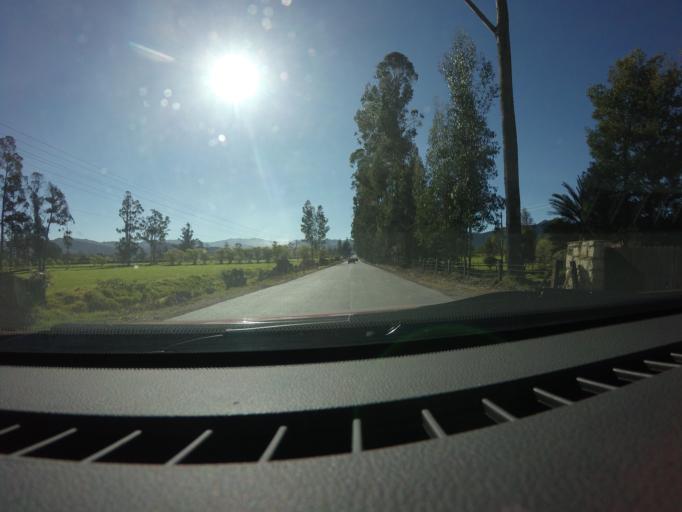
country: CO
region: Cundinamarca
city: Ubate
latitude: 5.2894
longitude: -73.8093
